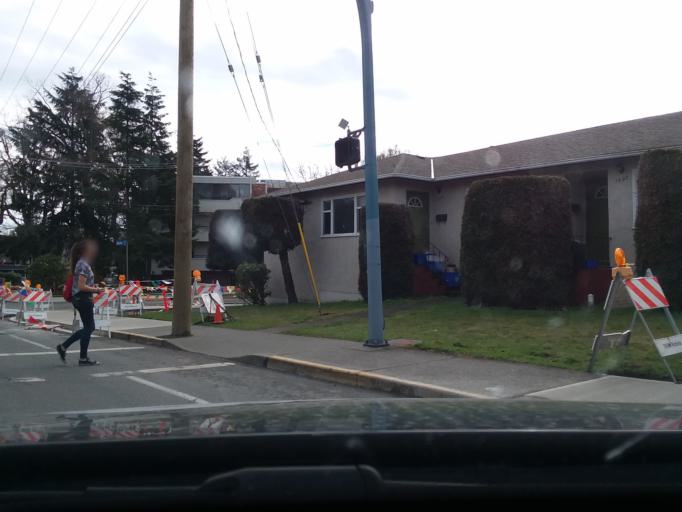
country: CA
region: British Columbia
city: Victoria
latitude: 48.4282
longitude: -123.3335
